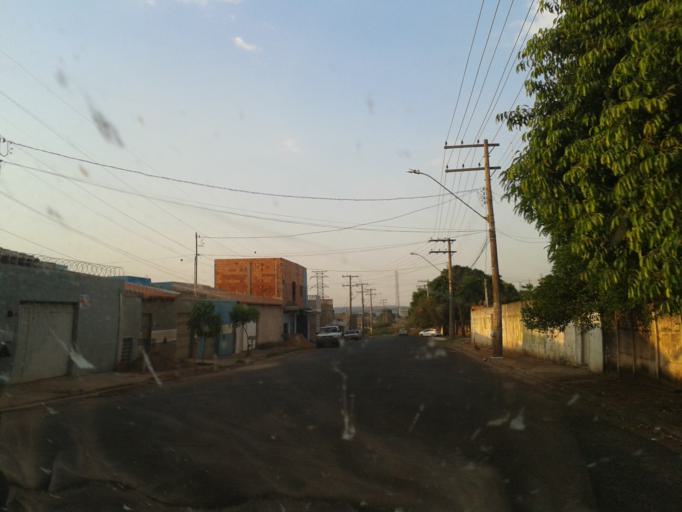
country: BR
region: Minas Gerais
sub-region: Uberlandia
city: Uberlandia
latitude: -18.9111
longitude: -48.3351
